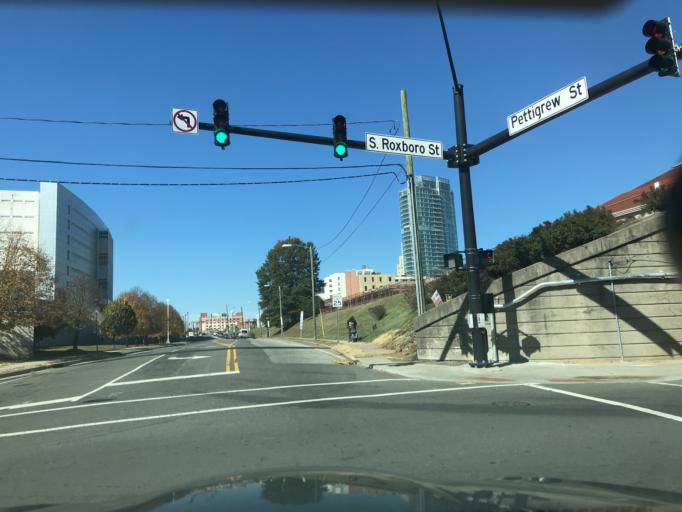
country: US
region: North Carolina
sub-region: Durham County
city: Durham
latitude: 35.9925
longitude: -78.8991
